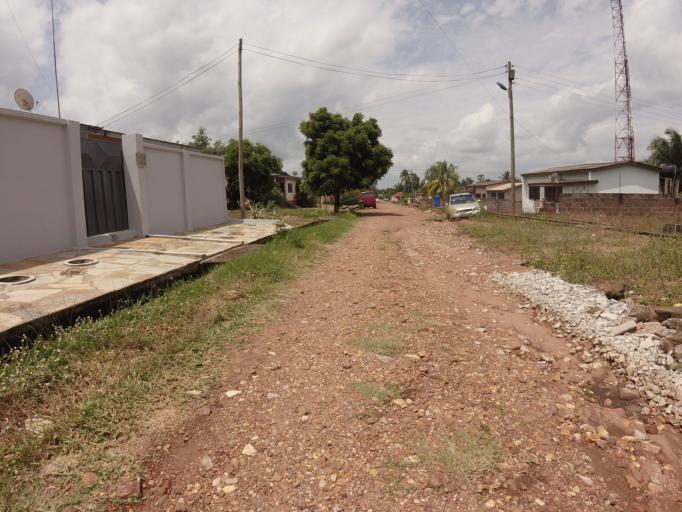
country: GH
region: Volta
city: Ho
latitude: 6.5907
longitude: 0.4750
